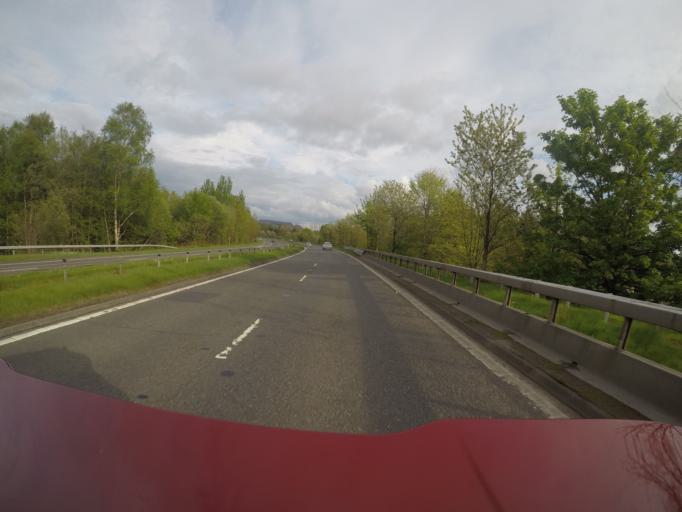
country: GB
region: Scotland
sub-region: West Dunbartonshire
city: Renton
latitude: 55.9624
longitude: -4.5852
